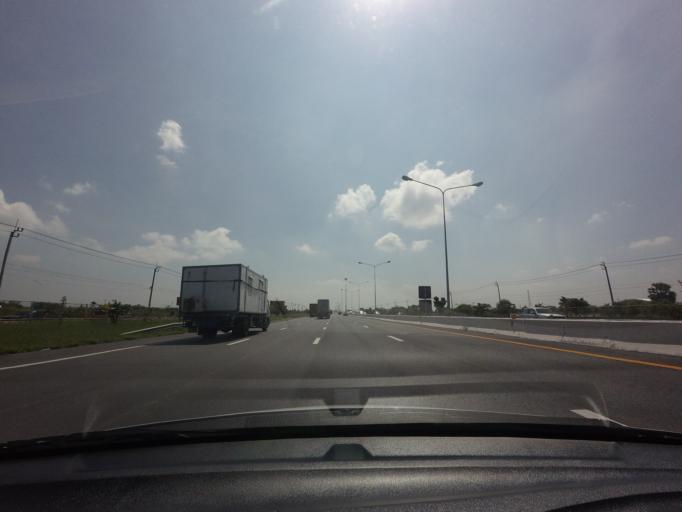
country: TH
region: Samut Prakan
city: Ban Khlong Bang Sao Thong
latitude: 13.6434
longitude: 100.8854
